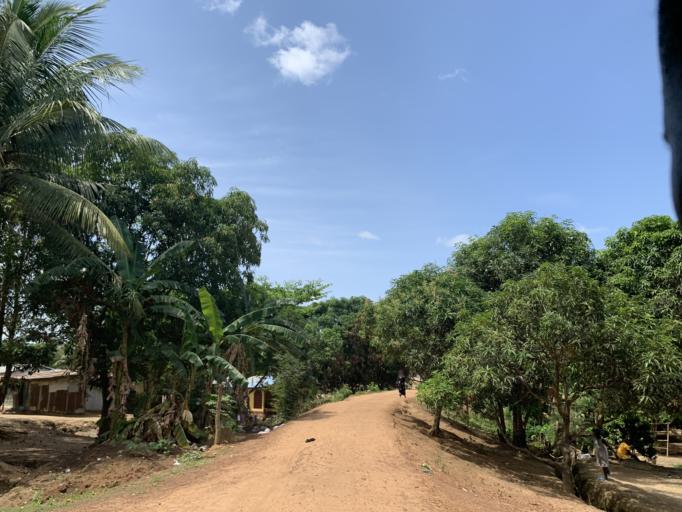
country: SL
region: Western Area
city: Waterloo
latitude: 8.3339
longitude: -13.0477
